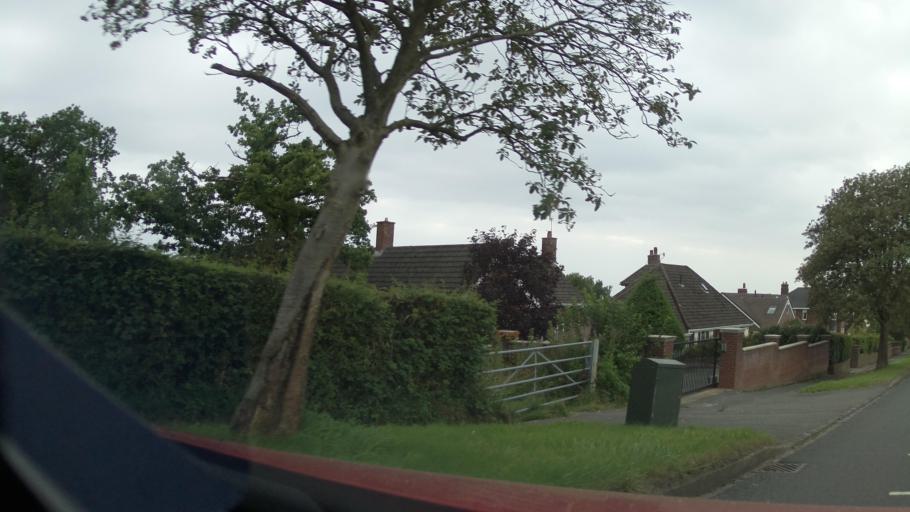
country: GB
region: England
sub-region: Staffordshire
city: Longton
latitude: 53.0211
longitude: -2.1122
